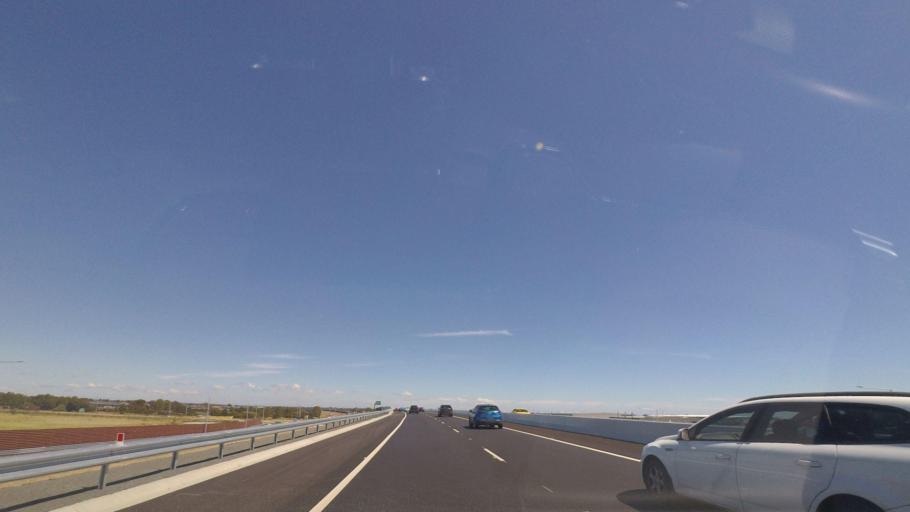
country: AU
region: Victoria
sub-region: Kingston
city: Waterways
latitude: -38.0073
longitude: 145.1226
